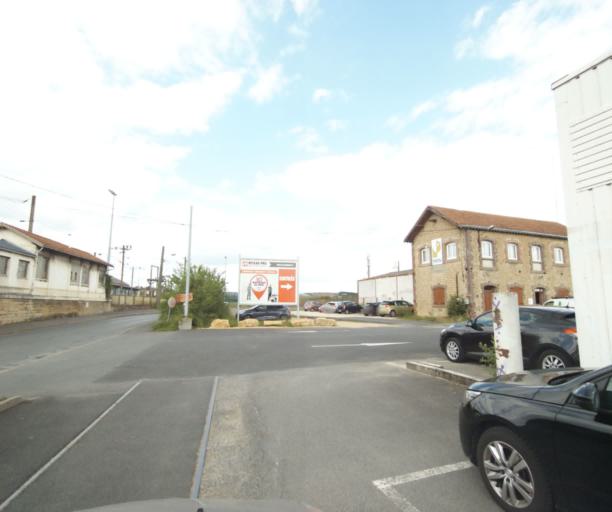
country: FR
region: Champagne-Ardenne
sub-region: Departement des Ardennes
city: Charleville-Mezieres
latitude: 49.7668
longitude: 4.7259
